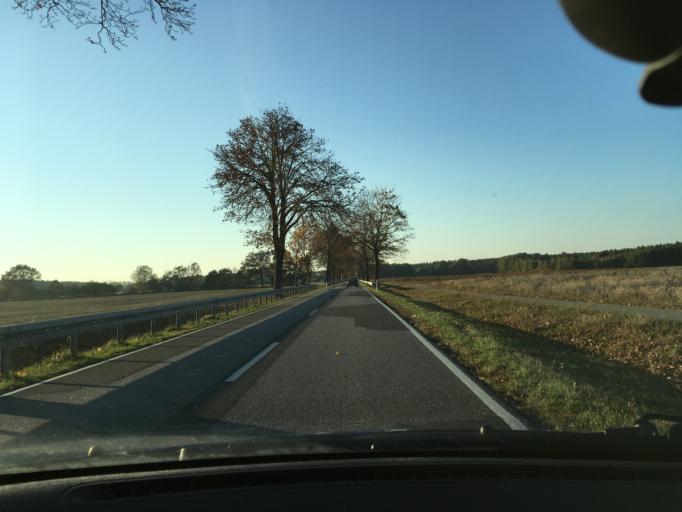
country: DE
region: Mecklenburg-Vorpommern
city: Boizenburg
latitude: 53.3550
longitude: 10.7991
